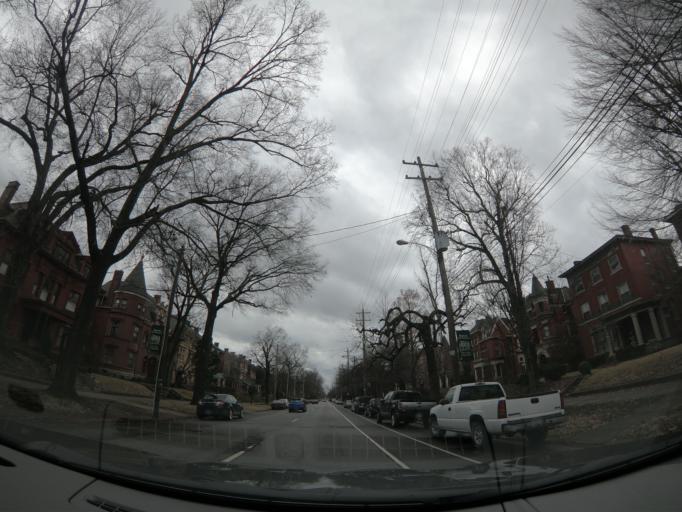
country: US
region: Kentucky
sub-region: Jefferson County
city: Louisville
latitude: 38.2304
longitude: -85.7595
